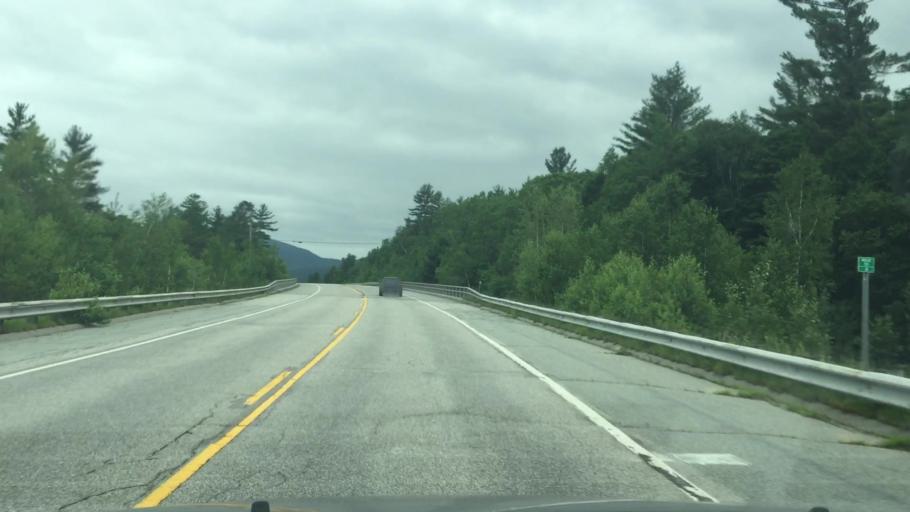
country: US
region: New Hampshire
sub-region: Carroll County
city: North Conway
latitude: 44.1143
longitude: -71.3541
